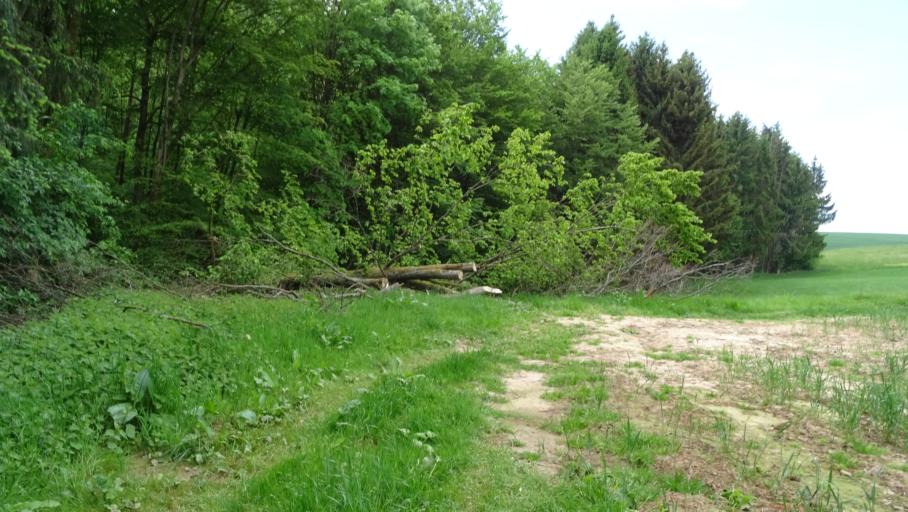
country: DE
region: Baden-Wuerttemberg
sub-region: Karlsruhe Region
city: Binau
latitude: 49.3751
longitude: 9.0529
